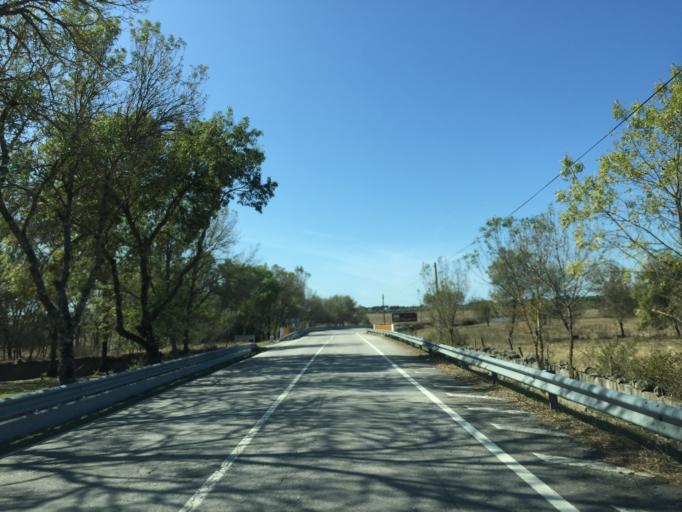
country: PT
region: Portalegre
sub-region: Portalegre
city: Alagoa
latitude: 39.4269
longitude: -7.5871
